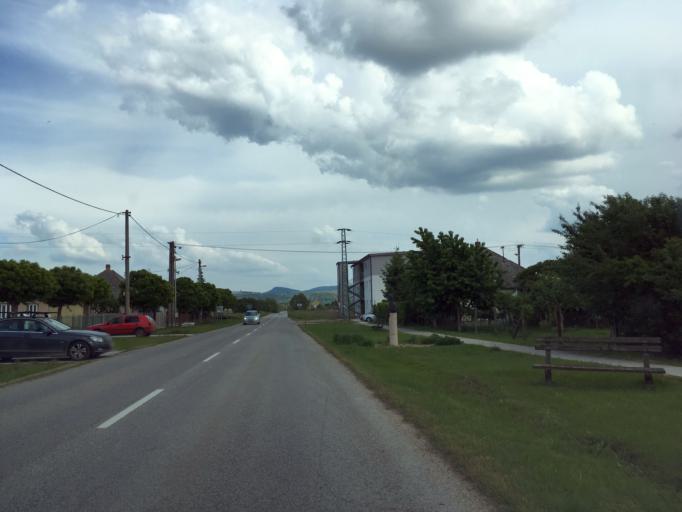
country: HU
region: Komarom-Esztergom
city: Dunaalmas
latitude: 47.7516
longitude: 18.3252
